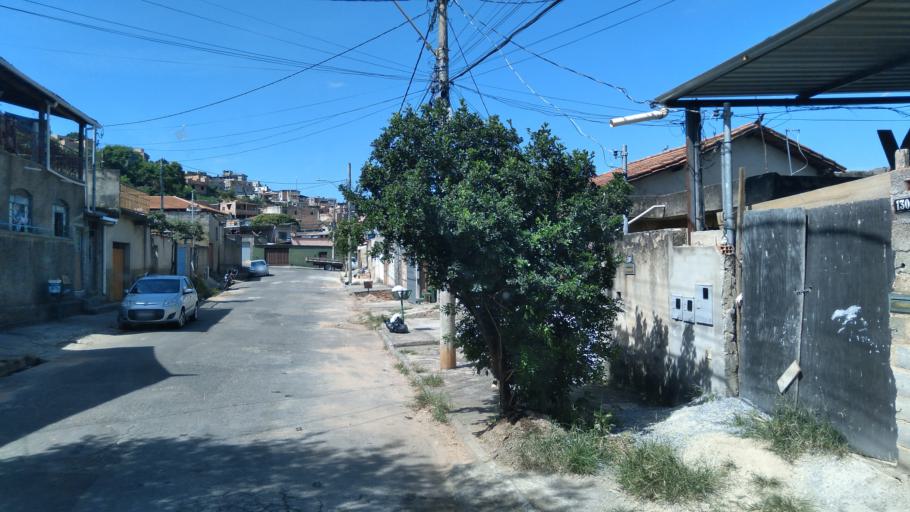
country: BR
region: Minas Gerais
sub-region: Belo Horizonte
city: Belo Horizonte
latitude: -19.8502
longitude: -43.9017
